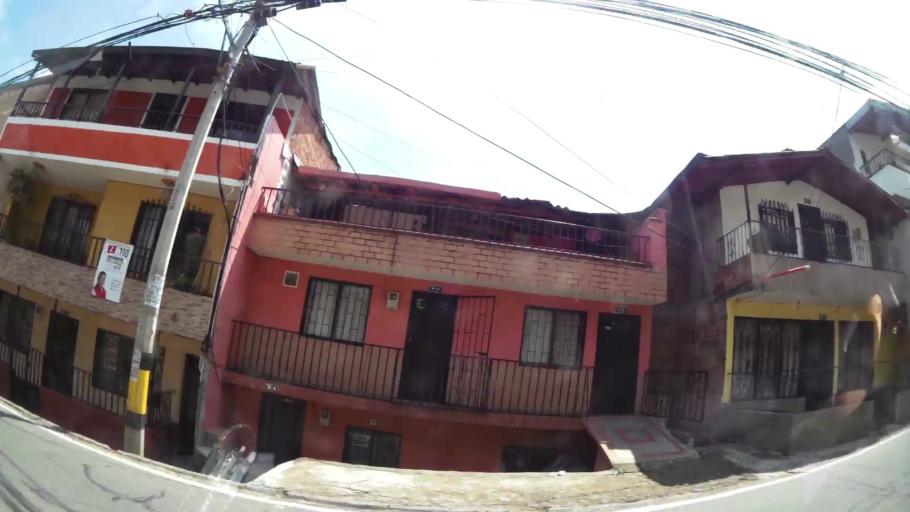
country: CO
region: Antioquia
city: La Estrella
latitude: 6.1866
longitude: -75.6503
